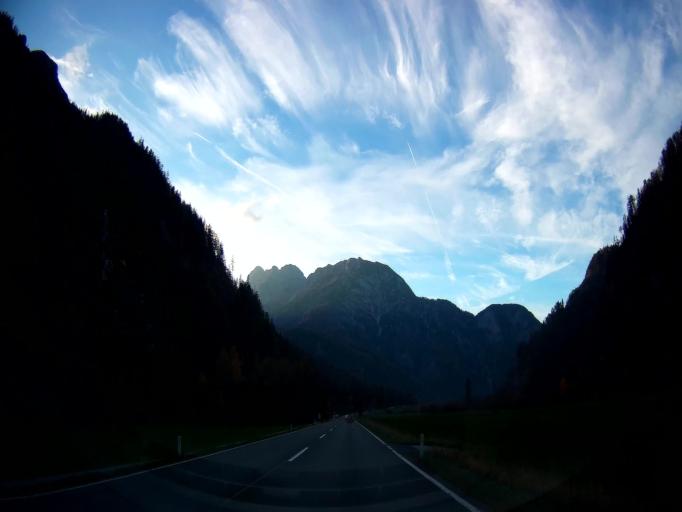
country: AT
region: Salzburg
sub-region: Politischer Bezirk Zell am See
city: Sankt Martin bei Lofer
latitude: 47.5254
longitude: 12.7437
